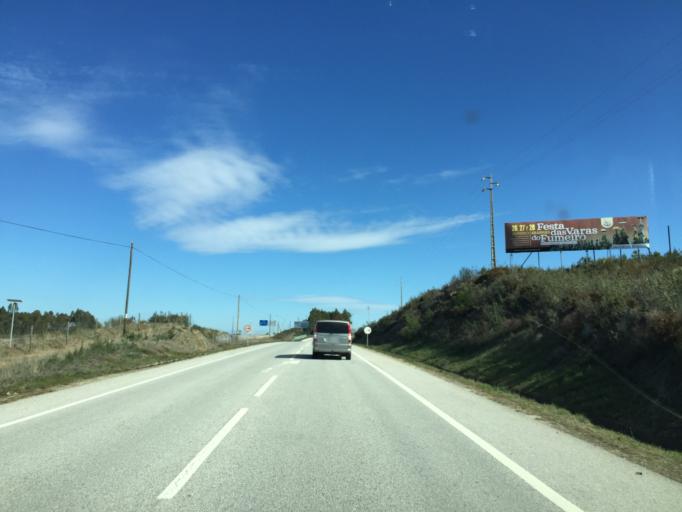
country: PT
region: Castelo Branco
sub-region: Castelo Branco
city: Castelo Branco
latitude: 39.7814
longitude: -7.5774
